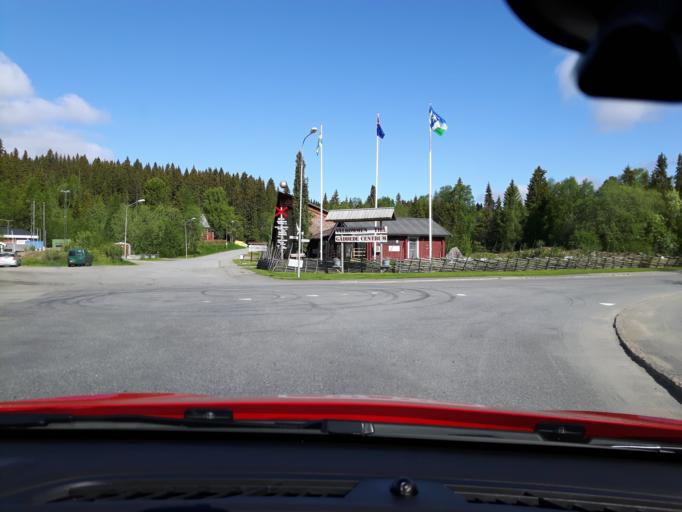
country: NO
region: Nord-Trondelag
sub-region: Lierne
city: Sandvika
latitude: 64.4996
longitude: 14.1424
